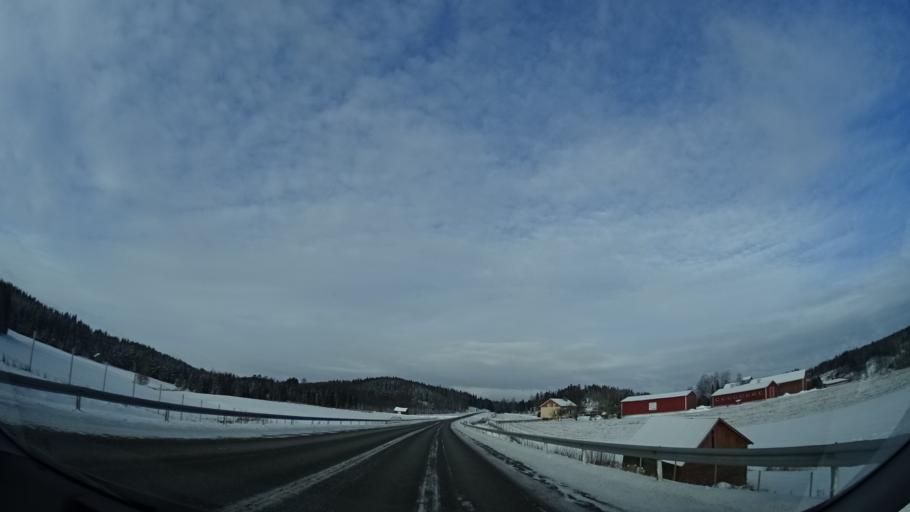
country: FI
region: Uusimaa
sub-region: Helsinki
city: Karkkila
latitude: 60.5727
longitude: 24.1542
